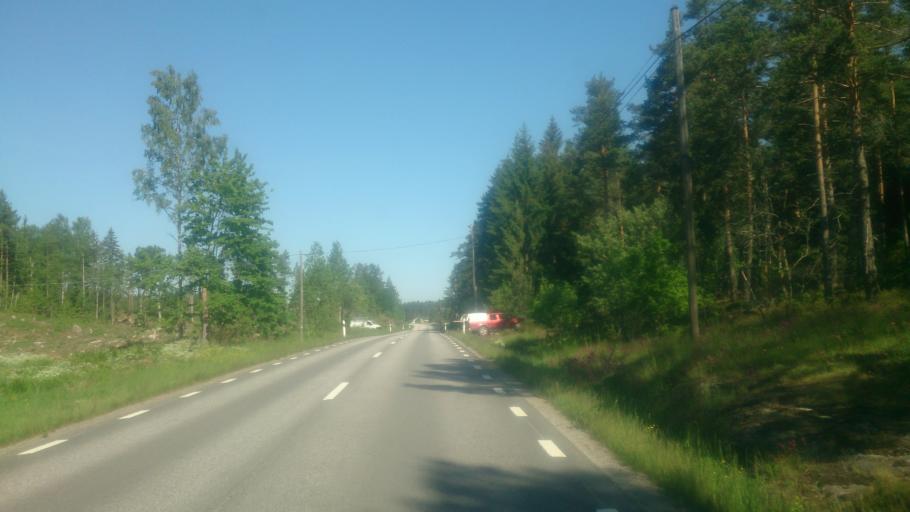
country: SE
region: OEstergoetland
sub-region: Atvidabergs Kommun
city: Atvidaberg
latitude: 58.1062
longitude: 16.1109
